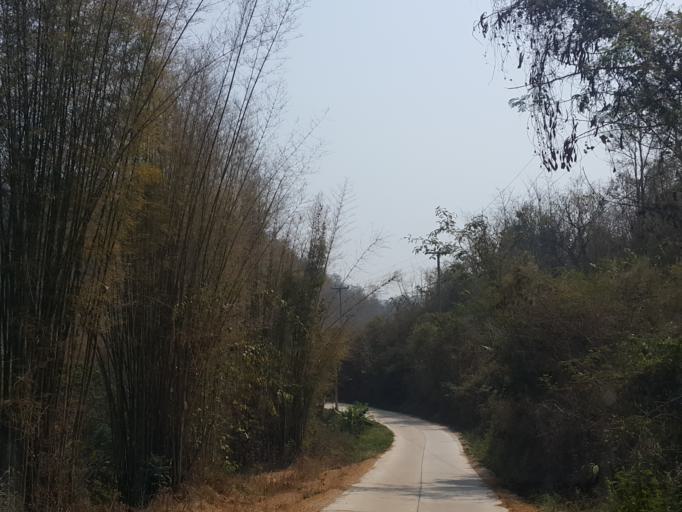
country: TH
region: Chiang Mai
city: Hang Dong
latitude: 18.7387
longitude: 98.8265
